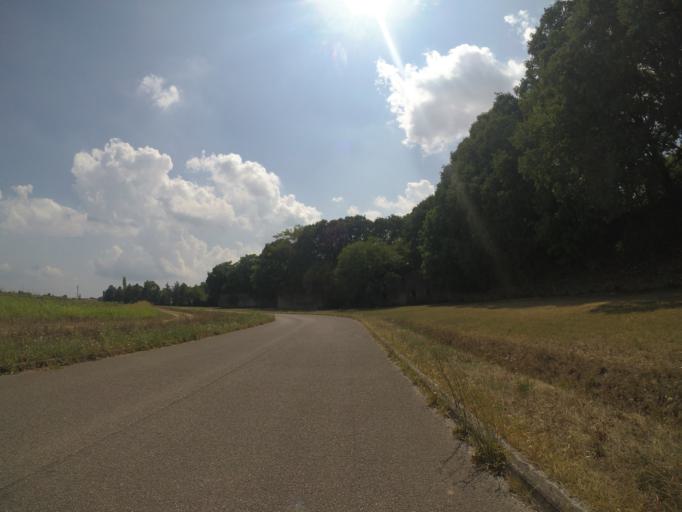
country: IT
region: Friuli Venezia Giulia
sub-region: Provincia di Udine
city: Codroipo
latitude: 45.9513
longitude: 13.0136
